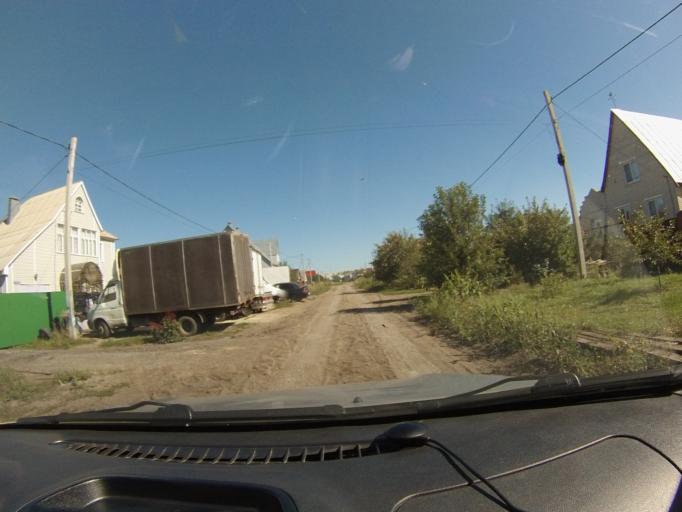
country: RU
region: Tambov
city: Komsomolets
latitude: 52.7607
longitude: 41.3658
